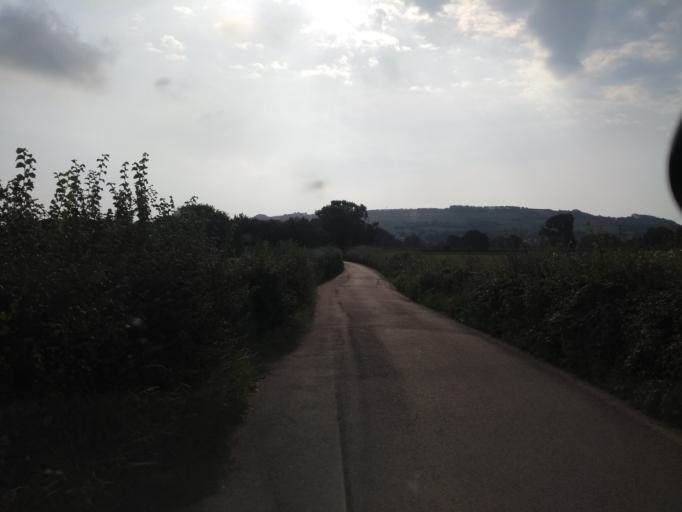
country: GB
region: England
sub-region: Devon
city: Colyton
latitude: 50.7525
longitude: -3.0459
